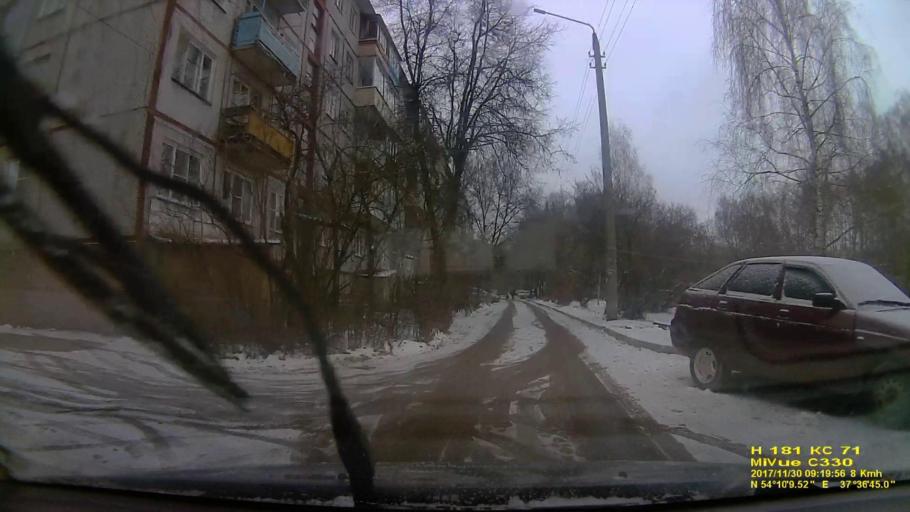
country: RU
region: Tula
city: Tula
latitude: 54.1693
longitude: 37.6127
